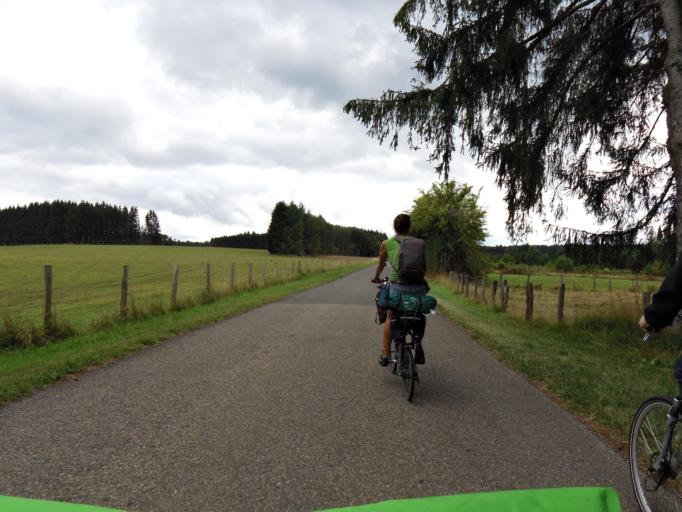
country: BE
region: Wallonia
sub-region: Province de Namur
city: Bievre
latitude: 49.9326
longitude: 5.0161
